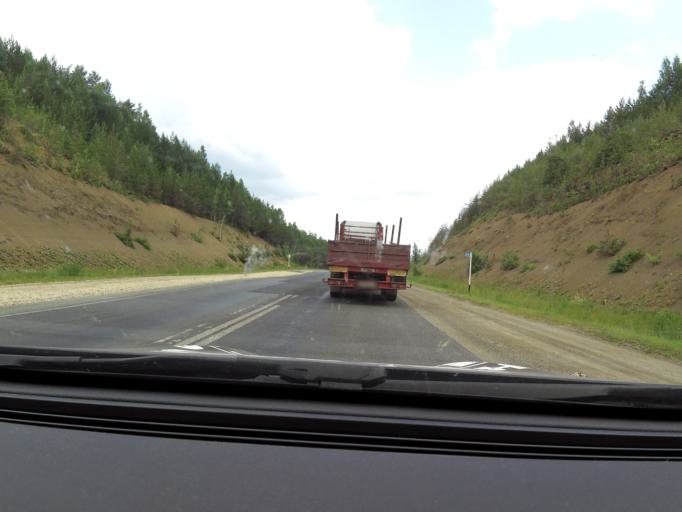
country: RU
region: Sverdlovsk
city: Ufimskiy
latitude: 56.7844
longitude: 58.3086
